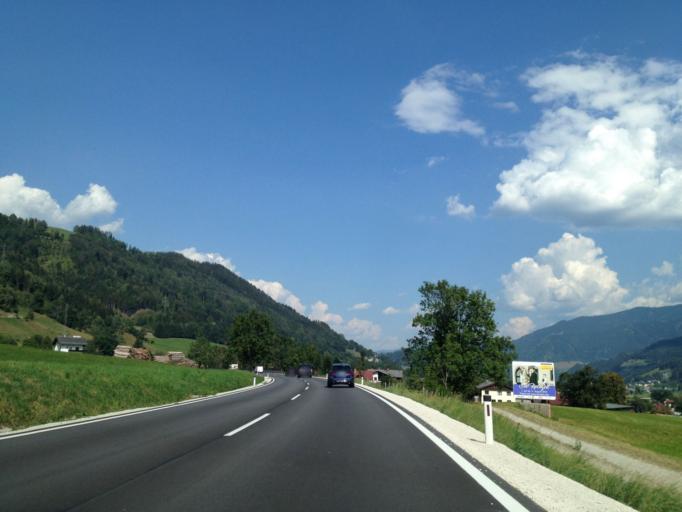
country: AT
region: Styria
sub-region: Politischer Bezirk Liezen
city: Pruggern
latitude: 47.4239
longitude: 13.8645
